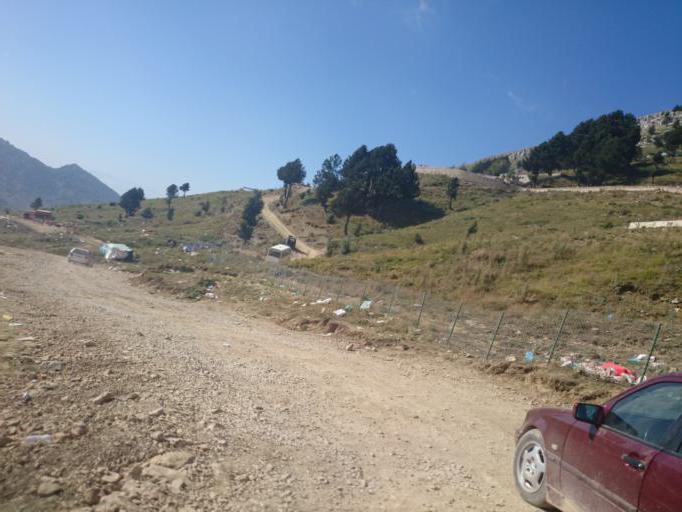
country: AL
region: Berat
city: Gjerbes
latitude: 40.6208
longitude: 20.1918
